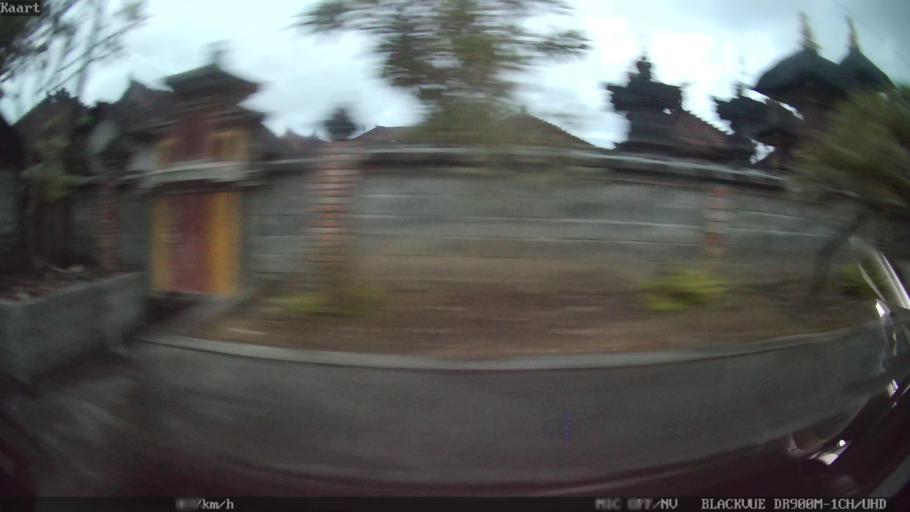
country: ID
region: Bali
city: Banjar Pasekan
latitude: -8.6186
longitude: 115.2739
